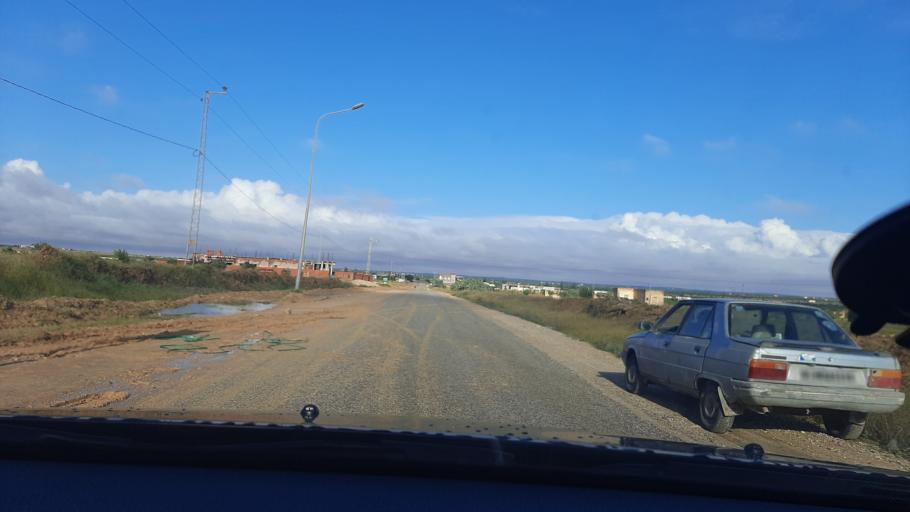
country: TN
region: Safaqis
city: Sfax
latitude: 34.8824
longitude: 10.6308
